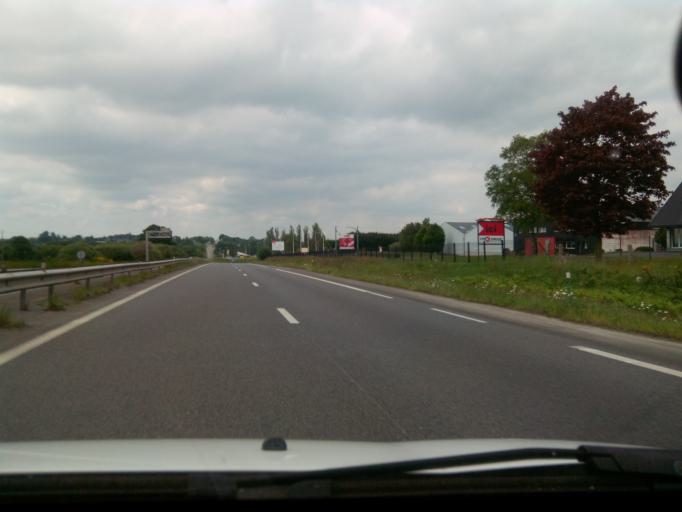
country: FR
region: Brittany
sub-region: Departement des Cotes-d'Armor
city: Broons
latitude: 48.3449
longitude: -2.2884
